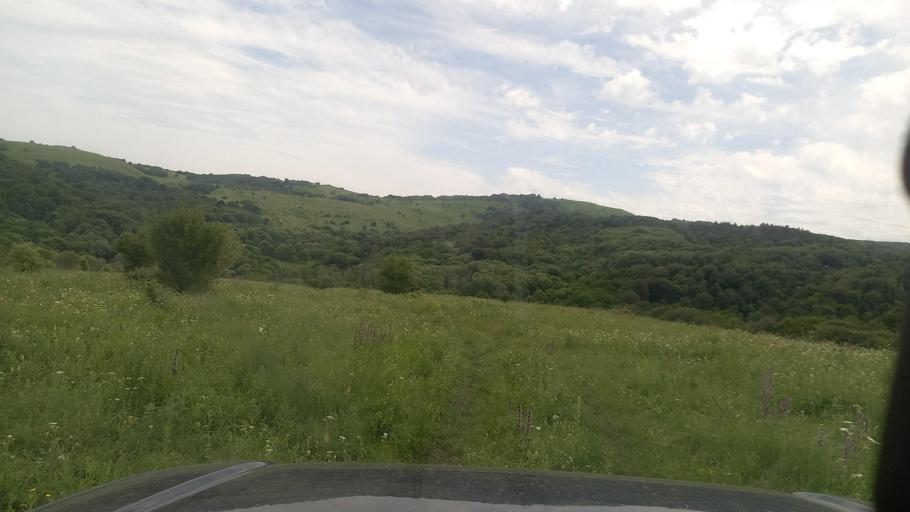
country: RU
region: Karachayevo-Cherkesiya
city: Pregradnaya
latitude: 44.0883
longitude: 41.1932
